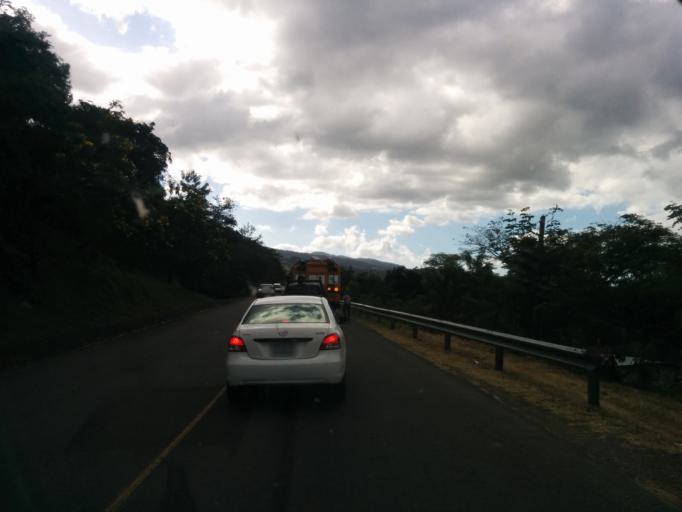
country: NI
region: Esteli
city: Esteli
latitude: 12.9992
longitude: -86.2856
